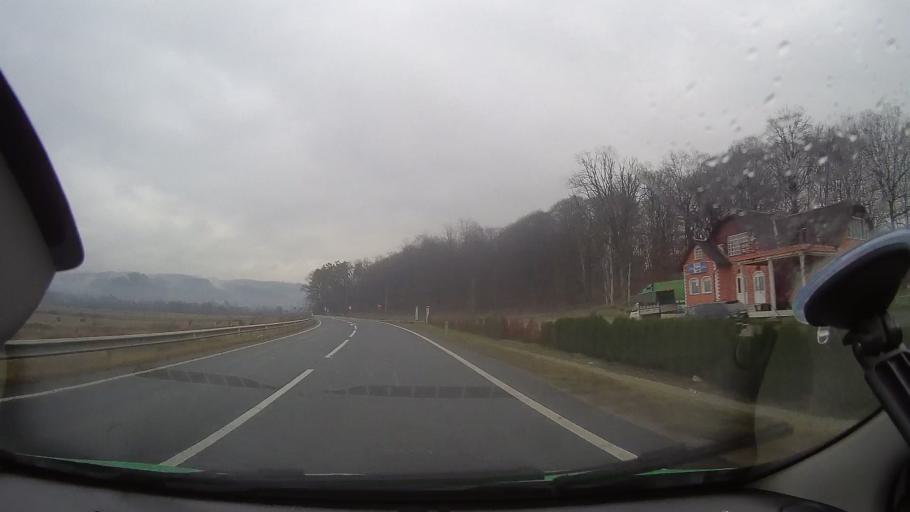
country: RO
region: Hunedoara
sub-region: Comuna Baia de Cris
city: Baia de Cris
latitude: 46.1771
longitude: 22.6960
